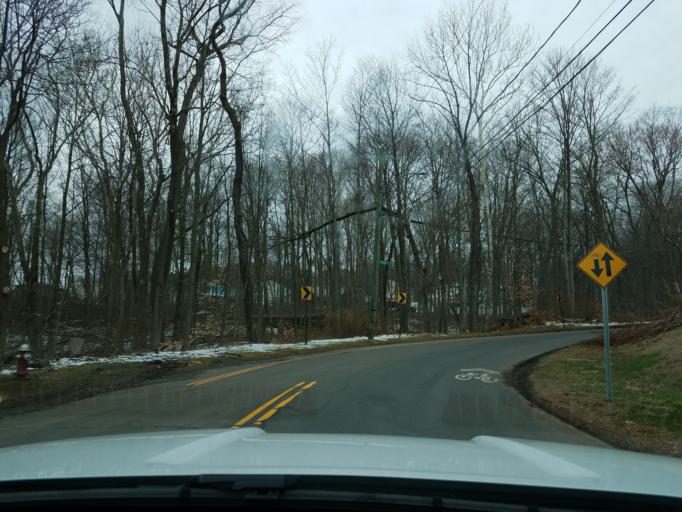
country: US
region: Connecticut
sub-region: Hartford County
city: New Britain
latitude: 41.6507
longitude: -72.7819
